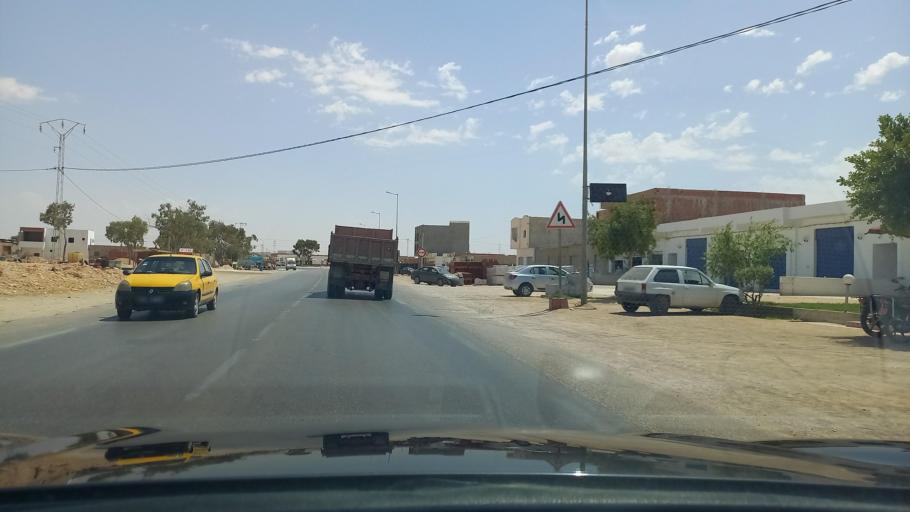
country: TN
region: Madanin
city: Medenine
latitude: 33.3704
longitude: 10.4487
